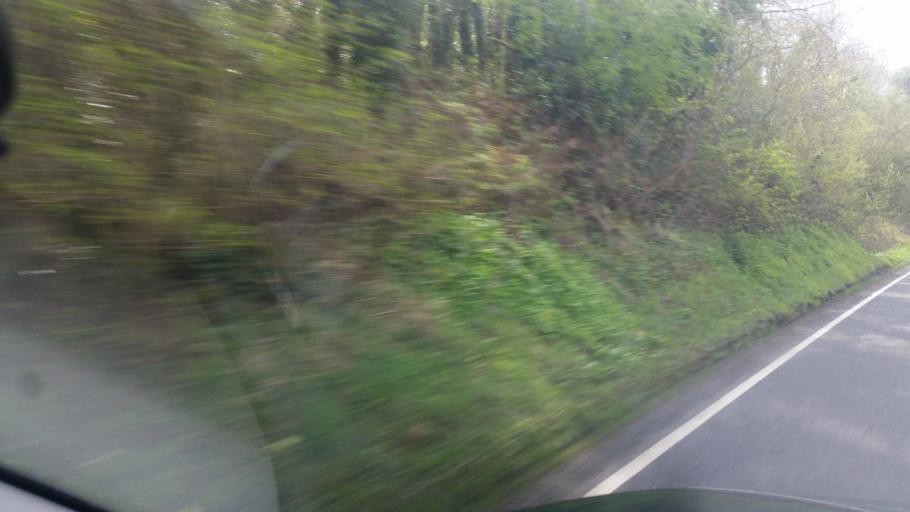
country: GB
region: Northern Ireland
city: Irvinestown
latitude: 54.4717
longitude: -7.8583
